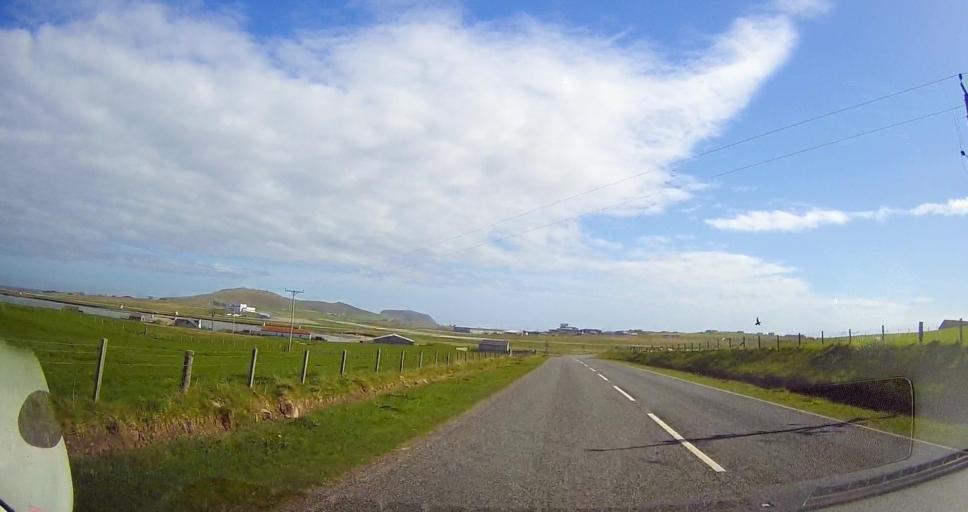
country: GB
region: Scotland
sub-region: Shetland Islands
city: Sandwick
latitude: 59.8864
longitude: -1.3030
